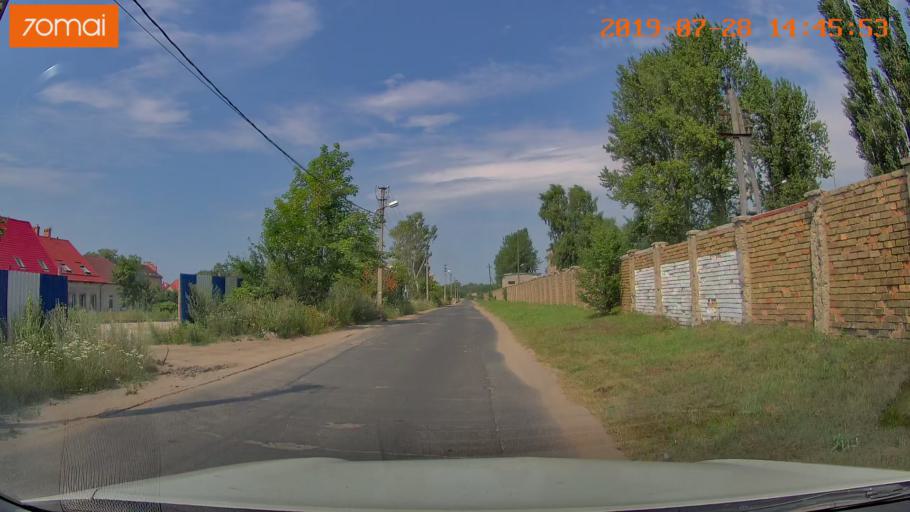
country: RU
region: Kaliningrad
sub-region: Gorod Kaliningrad
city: Yantarnyy
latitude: 54.8732
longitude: 19.9396
